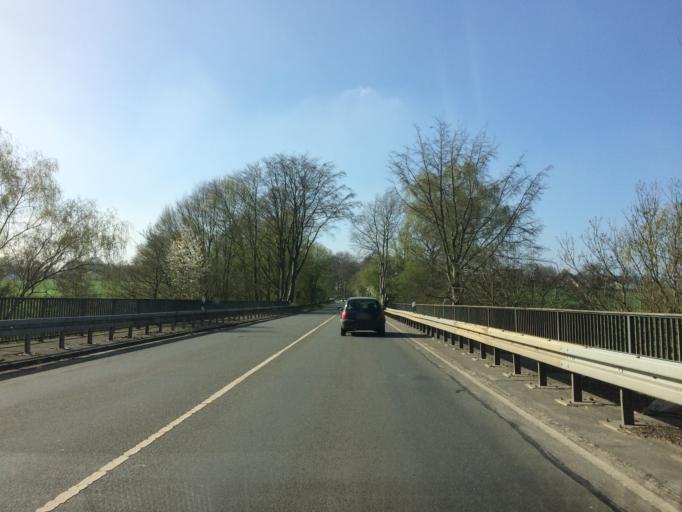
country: DE
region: North Rhine-Westphalia
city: Hattingen
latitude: 51.4402
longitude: 7.1809
